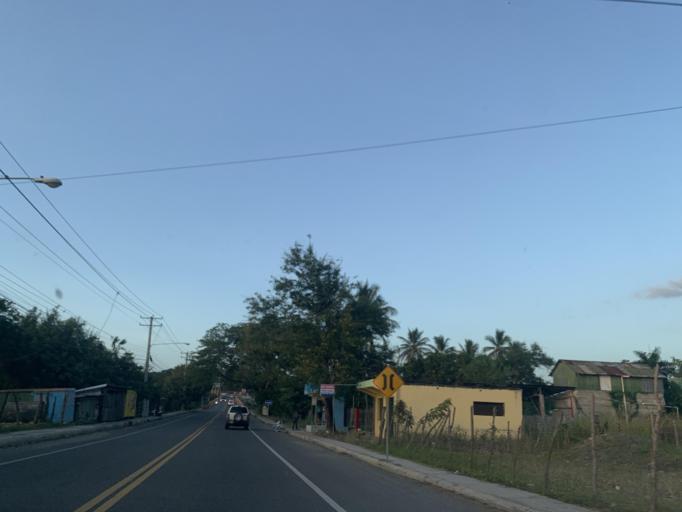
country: DO
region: Puerto Plata
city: Imbert
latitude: 19.7547
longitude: -70.8377
